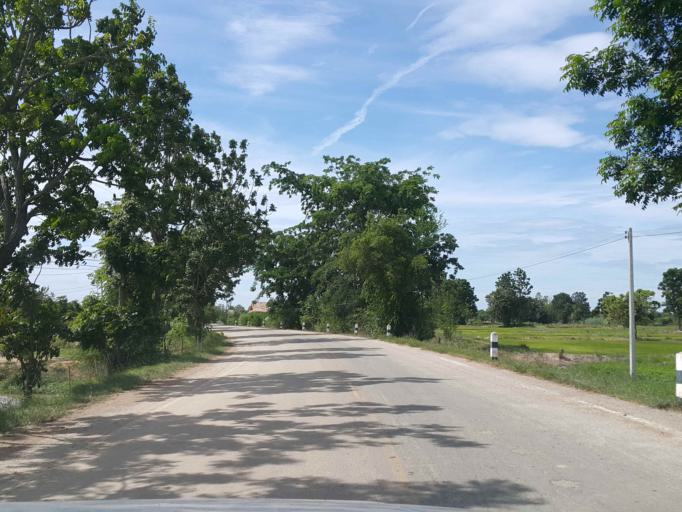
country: TH
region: Sukhothai
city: Ban Dan Lan Hoi
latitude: 17.1482
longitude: 99.5218
